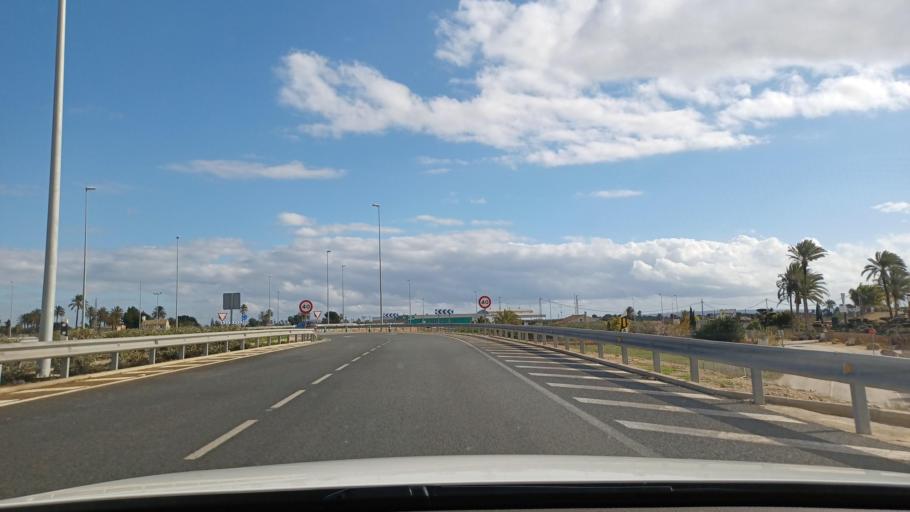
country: ES
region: Valencia
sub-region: Provincia de Alicante
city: Elche
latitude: 38.2614
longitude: -0.6606
